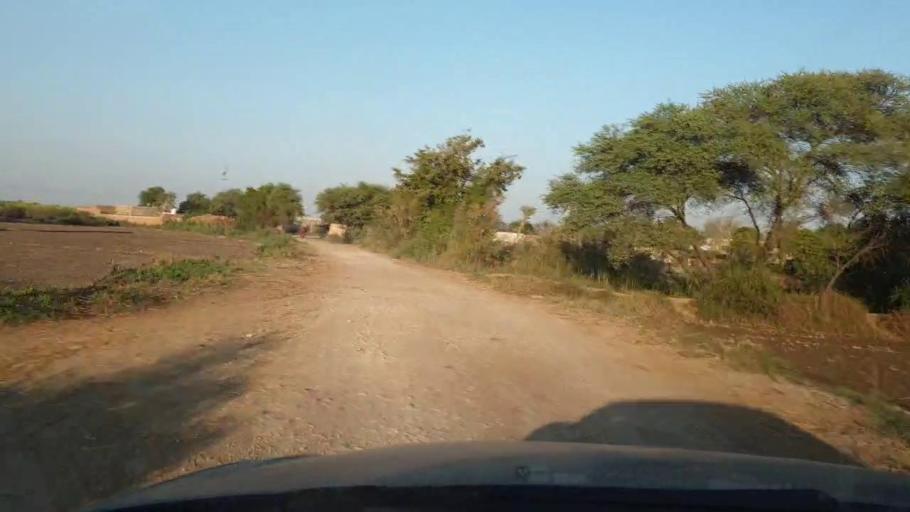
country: PK
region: Sindh
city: Matli
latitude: 25.0348
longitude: 68.6275
